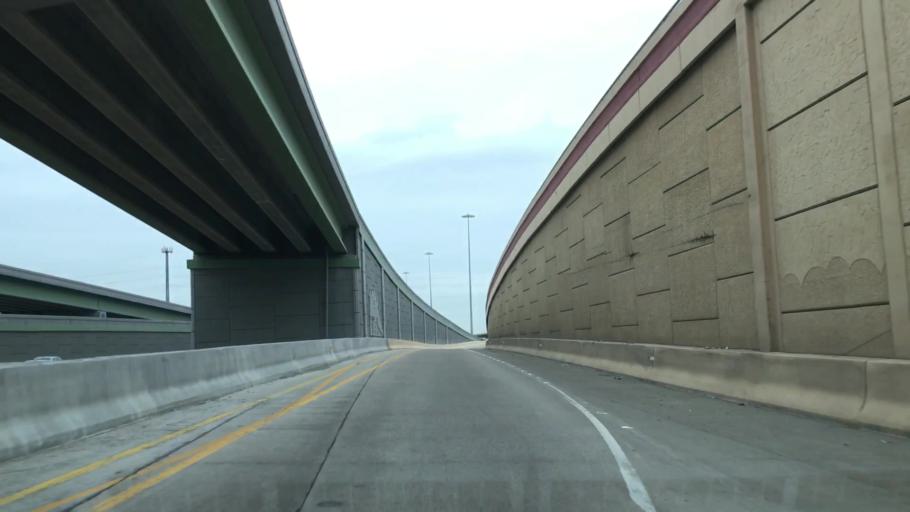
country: US
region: Texas
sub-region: Dallas County
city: Irving
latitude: 32.8411
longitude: -96.9142
